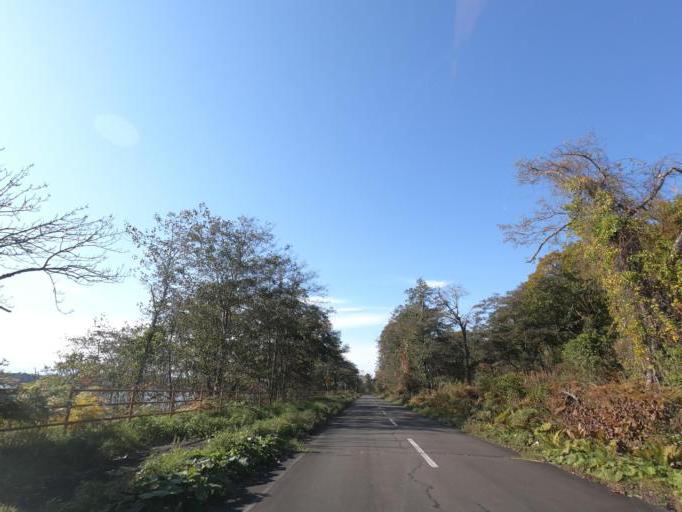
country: JP
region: Hokkaido
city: Obihiro
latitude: 42.6083
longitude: 143.5481
